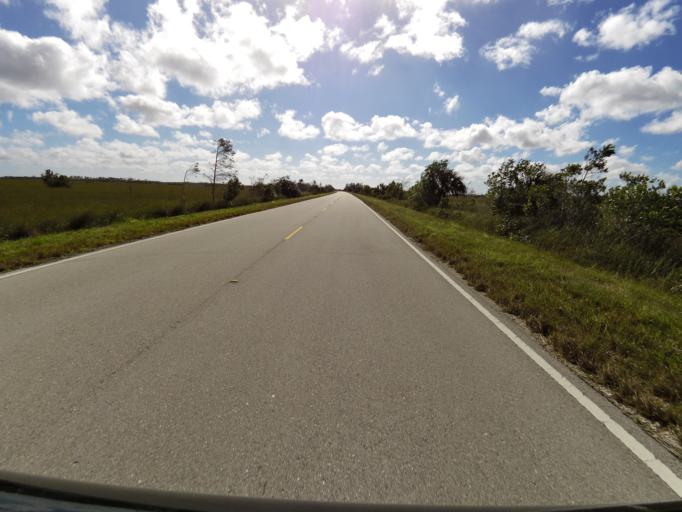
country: US
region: Florida
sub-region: Miami-Dade County
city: Florida City
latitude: 25.3734
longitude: -80.8155
